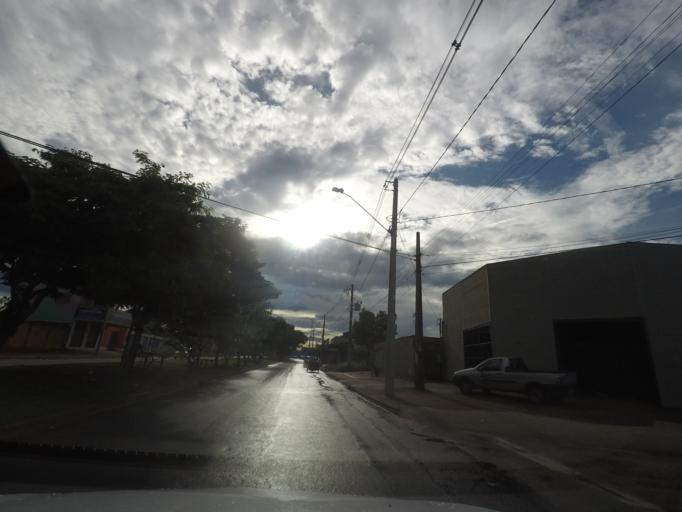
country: BR
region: Goias
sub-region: Aparecida De Goiania
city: Aparecida de Goiania
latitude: -16.7611
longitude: -49.3525
